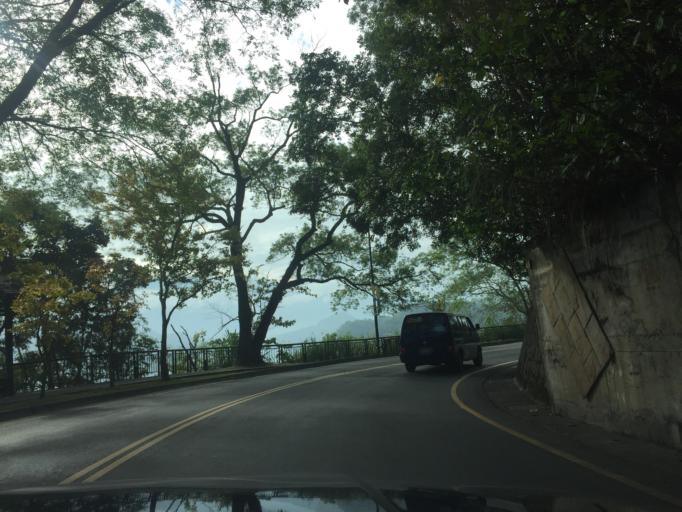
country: TW
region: Taiwan
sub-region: Nantou
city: Puli
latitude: 23.8630
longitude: 120.9042
